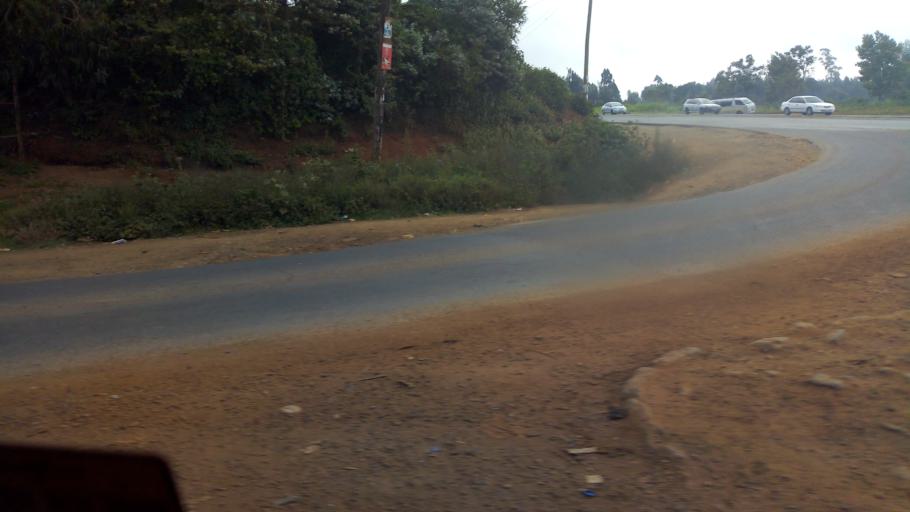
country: KE
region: Kiambu
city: Limuru
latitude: -1.1347
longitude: 36.6351
